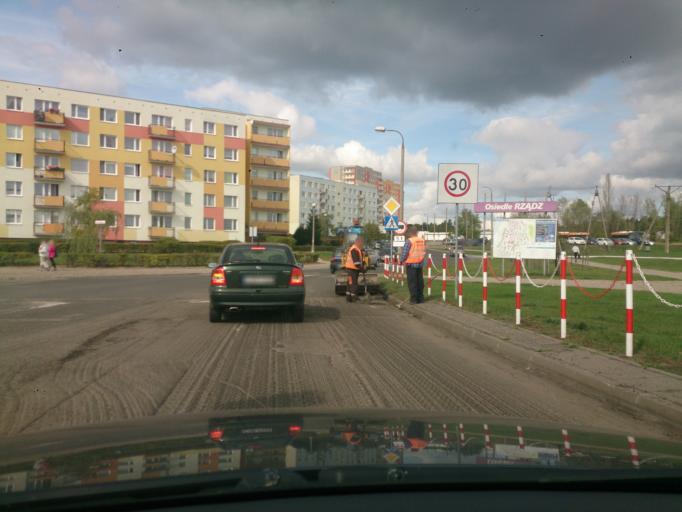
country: PL
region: Kujawsko-Pomorskie
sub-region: Grudziadz
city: Grudziadz
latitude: 53.4531
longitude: 18.7213
